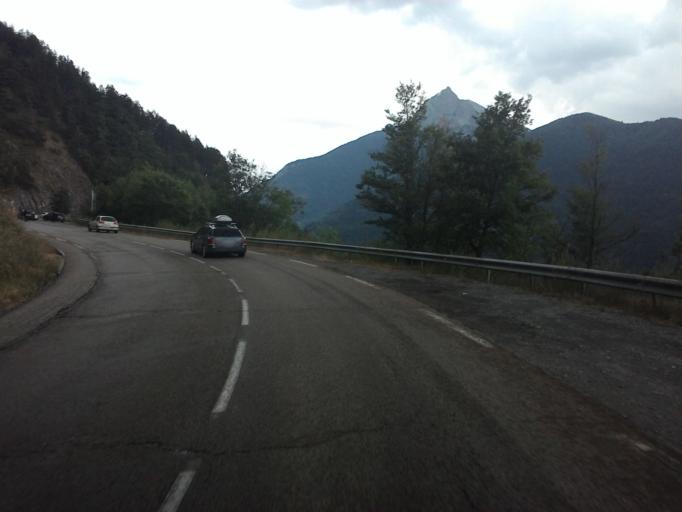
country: FR
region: Provence-Alpes-Cote d'Azur
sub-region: Departement des Hautes-Alpes
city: Saint-Bonnet-en-Champsaur
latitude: 44.8111
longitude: 5.9494
